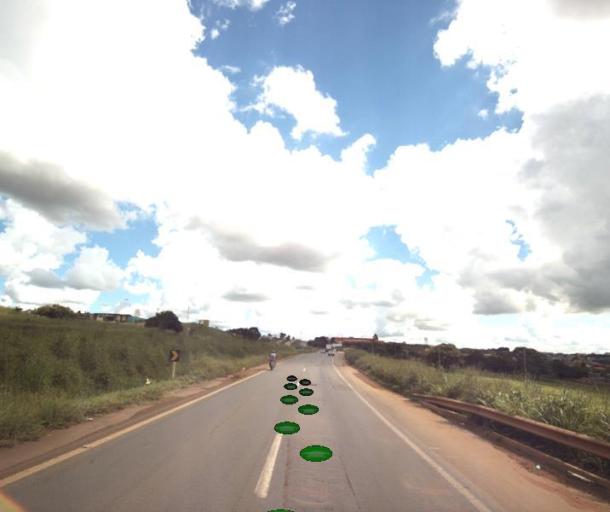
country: BR
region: Goias
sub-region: Anapolis
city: Anapolis
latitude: -16.3638
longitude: -48.9351
